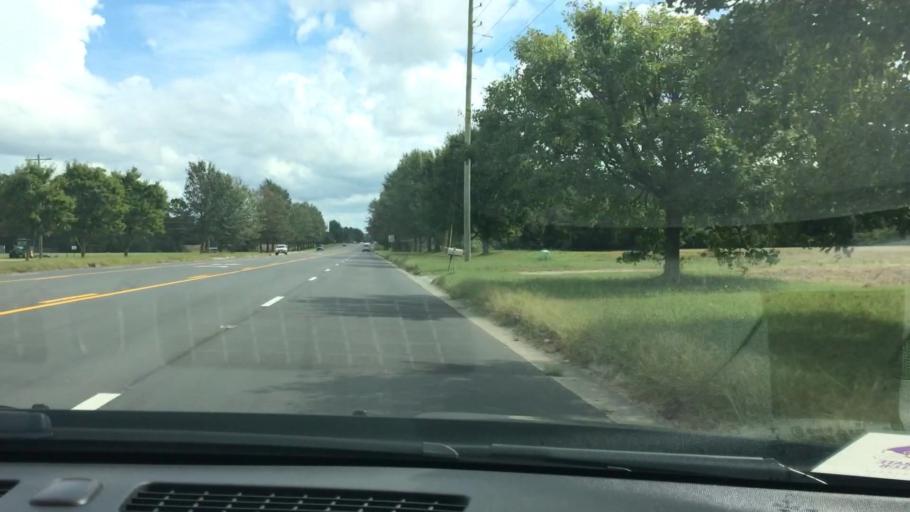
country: US
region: North Carolina
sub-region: Pitt County
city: Farmville
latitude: 35.5861
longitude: -77.6037
